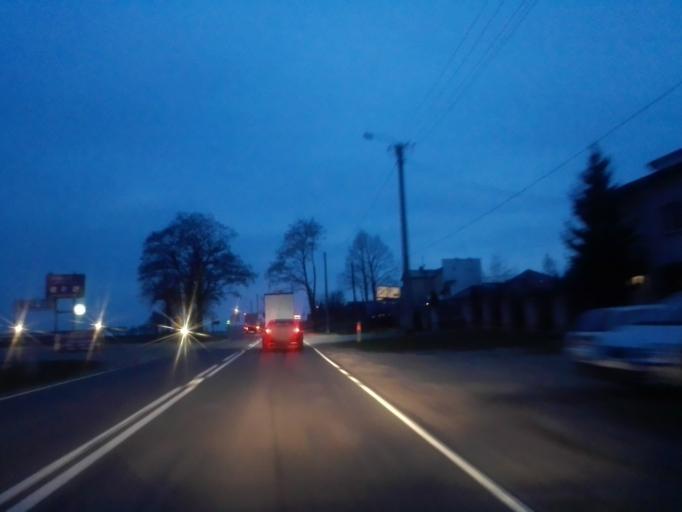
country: PL
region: Podlasie
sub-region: Lomza
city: Lomza
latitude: 53.1244
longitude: 22.0349
